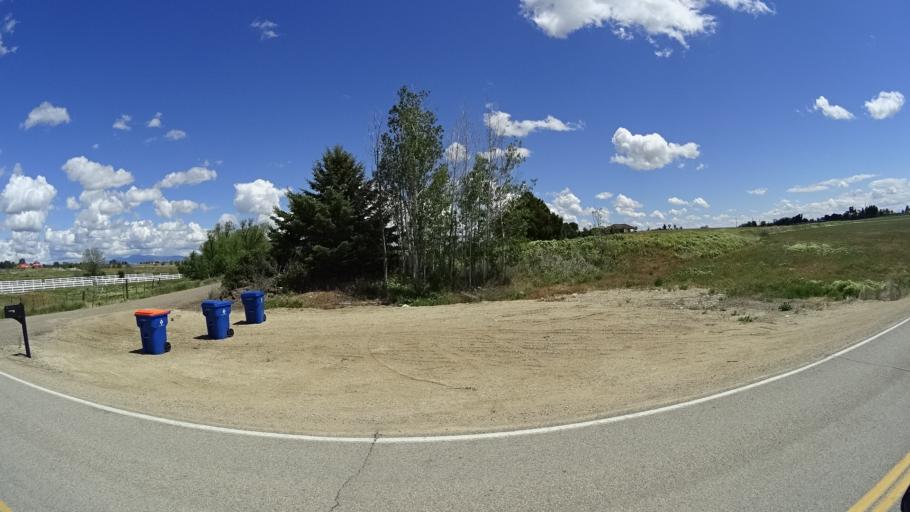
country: US
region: Idaho
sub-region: Ada County
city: Kuna
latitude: 43.5561
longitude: -116.4536
